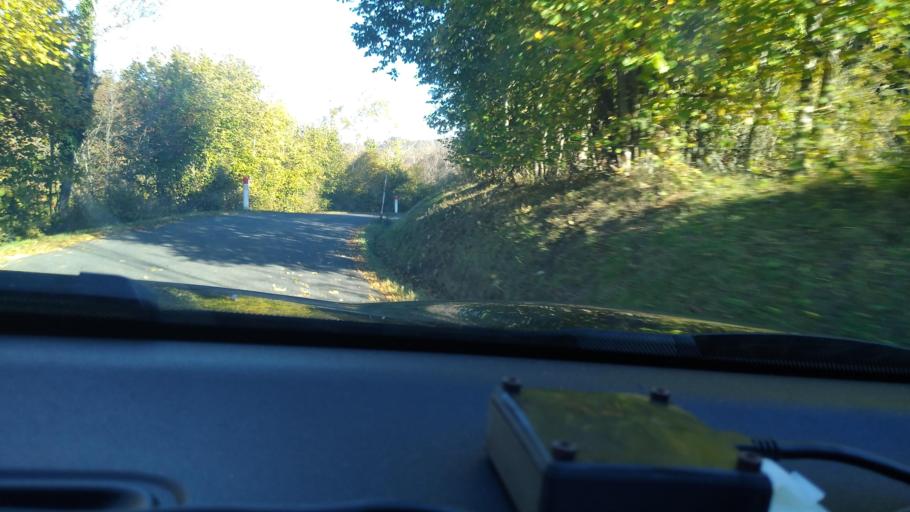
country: FR
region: Languedoc-Roussillon
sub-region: Departement de l'Aude
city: Quillan
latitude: 42.7361
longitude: 2.1279
